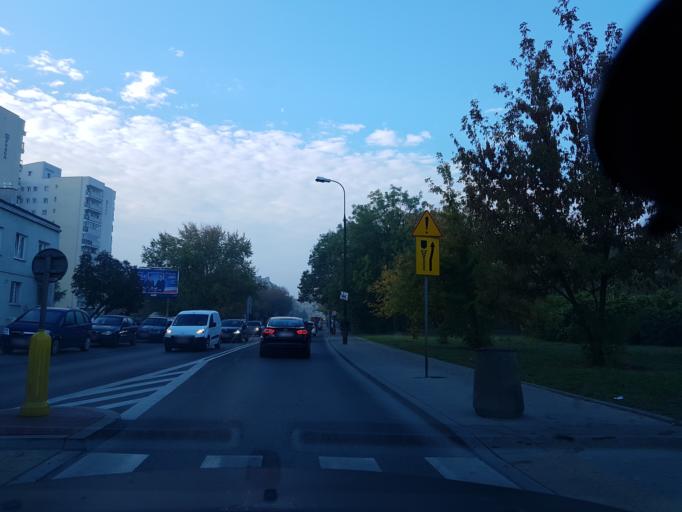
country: PL
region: Masovian Voivodeship
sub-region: Warszawa
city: Targowek
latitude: 52.2727
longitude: 21.0428
